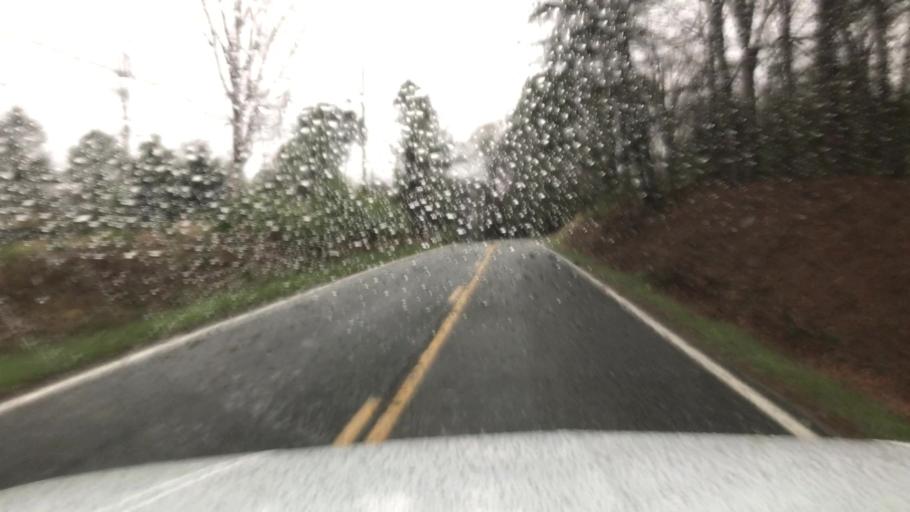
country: US
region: Virginia
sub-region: Henrico County
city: Short Pump
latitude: 37.6445
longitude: -77.6794
